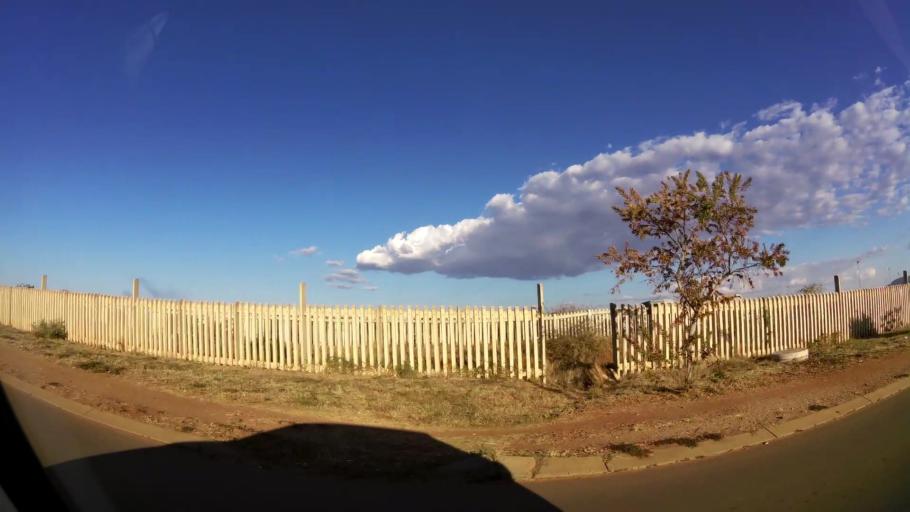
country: ZA
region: Limpopo
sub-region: Waterberg District Municipality
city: Mokopane
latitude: -24.1451
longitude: 28.9894
